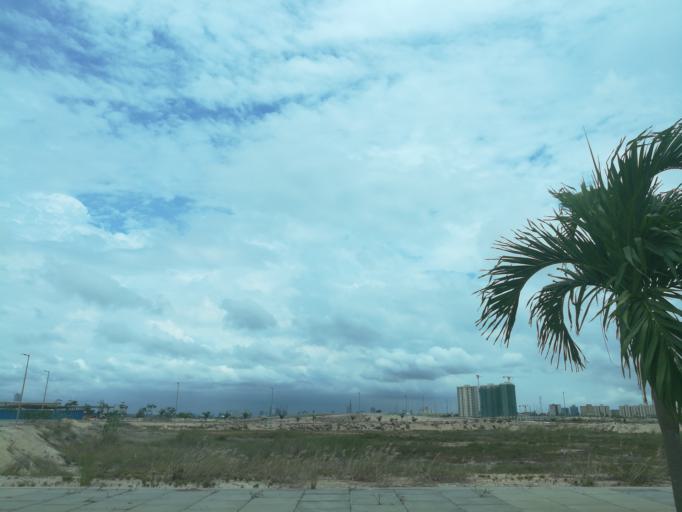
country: NG
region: Lagos
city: Lagos
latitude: 6.4089
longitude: 3.4124
